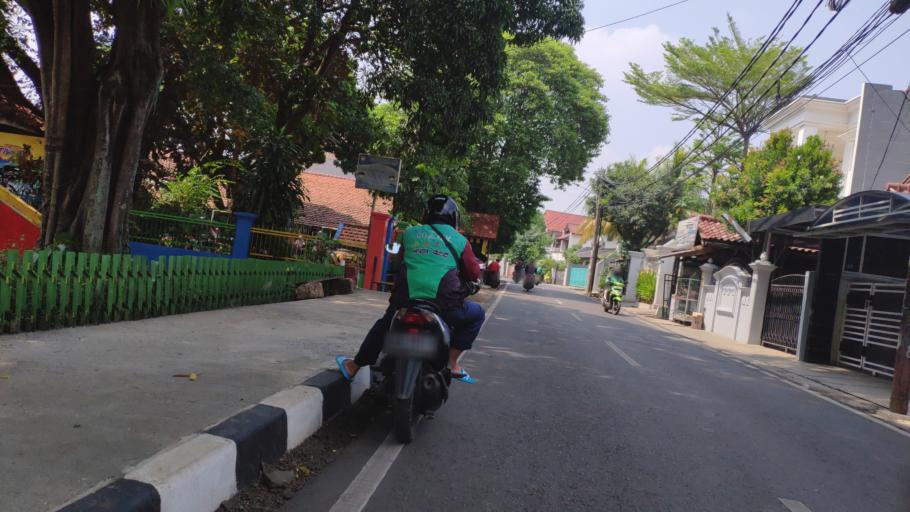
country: ID
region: West Java
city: Pamulang
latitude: -6.3038
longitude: 106.7991
